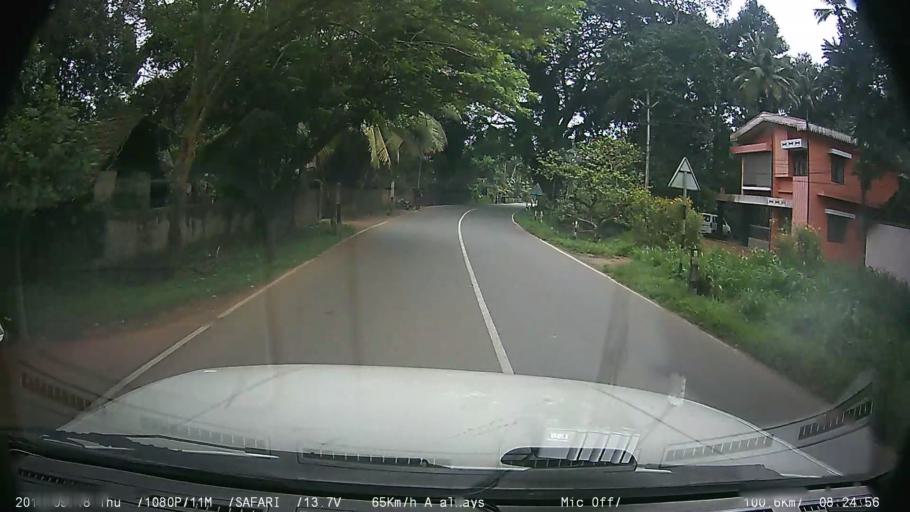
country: IN
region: Kerala
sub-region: Kottayam
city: Palackattumala
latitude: 9.6778
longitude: 76.6092
